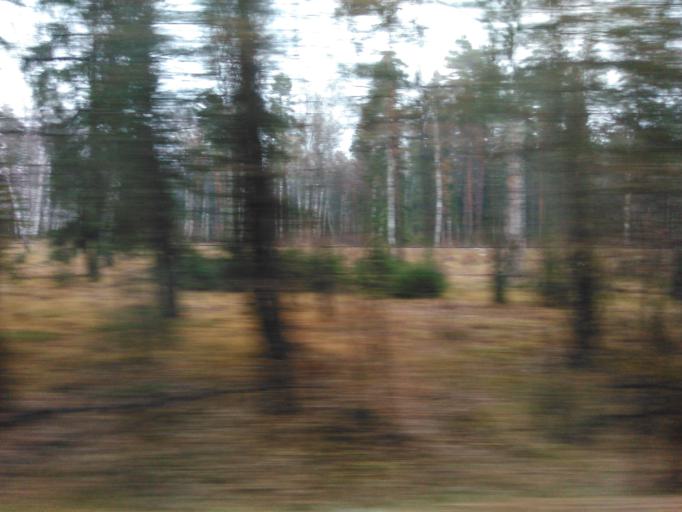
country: RU
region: Tatarstan
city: Osinovo
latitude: 55.8317
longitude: 48.8928
